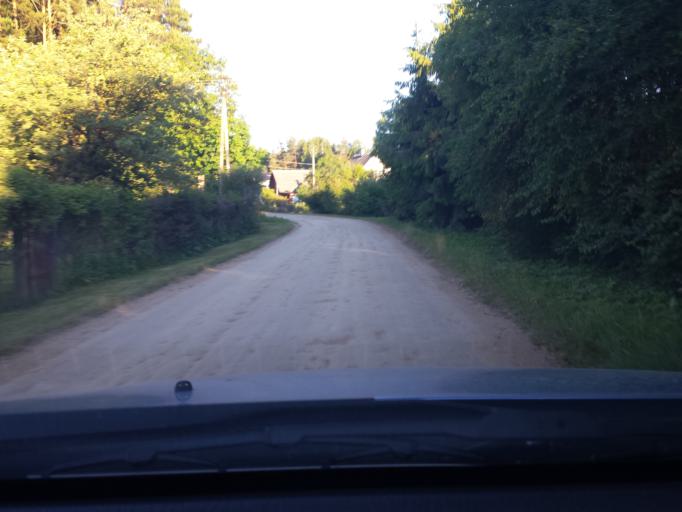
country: LV
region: Carnikava
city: Carnikava
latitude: 57.1230
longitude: 24.2369
